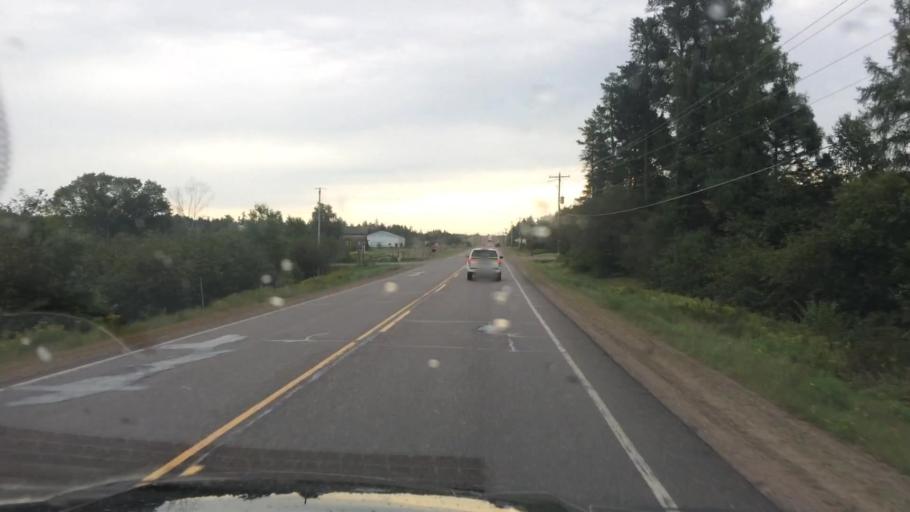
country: US
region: Wisconsin
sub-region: Lincoln County
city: Tomahawk
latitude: 45.4962
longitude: -89.7097
